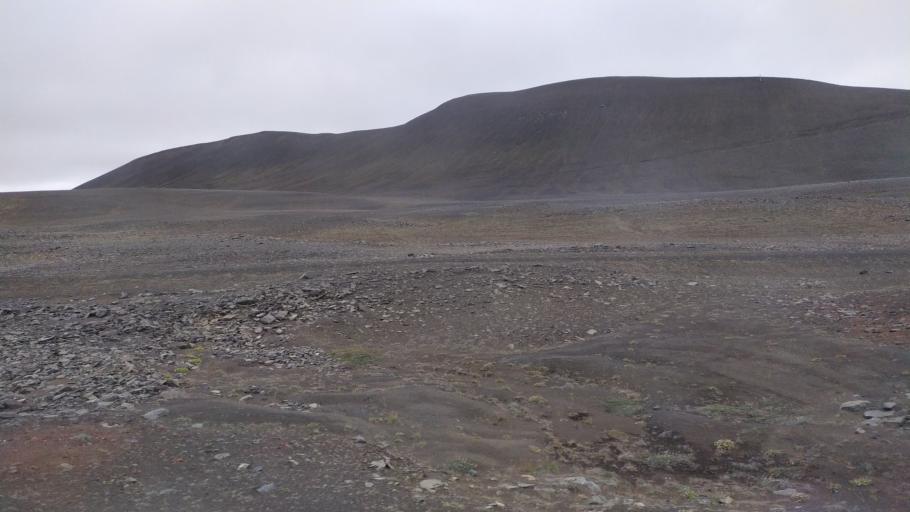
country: IS
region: Northeast
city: Laugar
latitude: 65.5675
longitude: -16.0363
